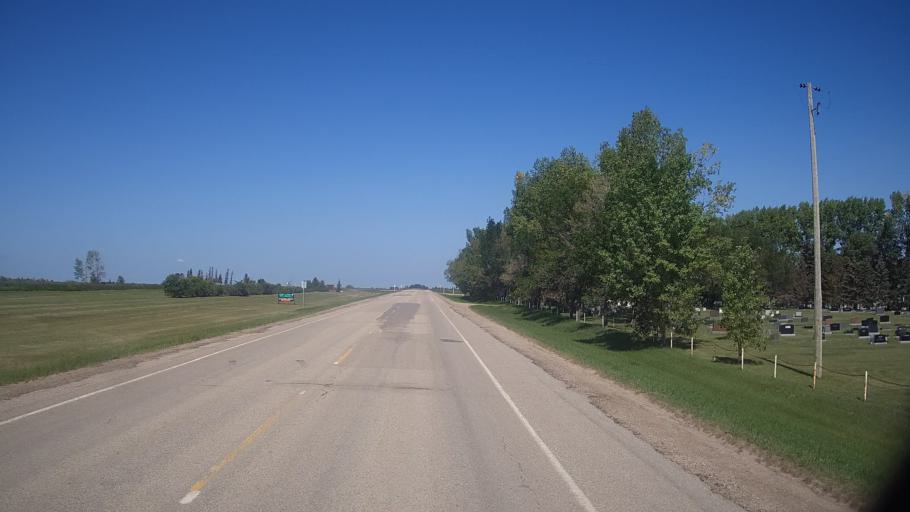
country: CA
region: Saskatchewan
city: Saskatoon
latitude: 51.8952
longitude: -106.0626
